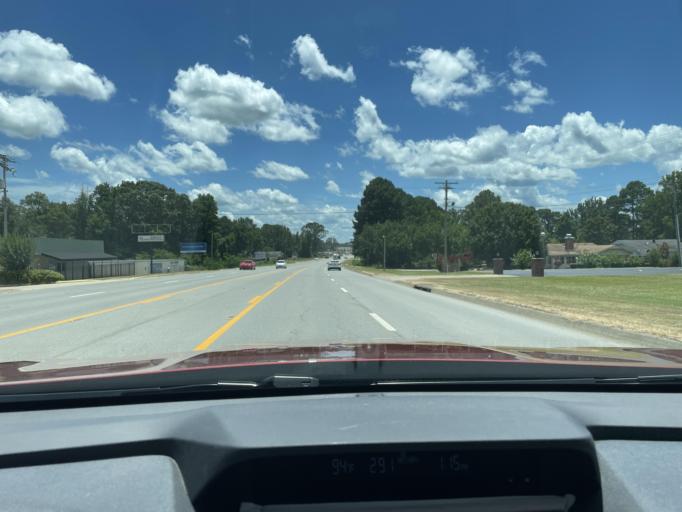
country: US
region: Arkansas
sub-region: Drew County
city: Monticello
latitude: 33.6456
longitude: -91.8011
